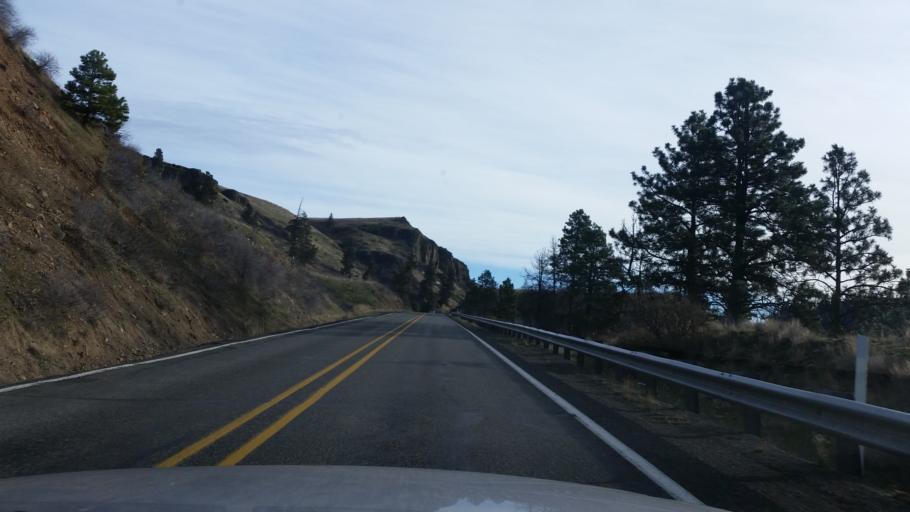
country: US
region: Washington
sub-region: Kittitas County
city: Cle Elum
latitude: 47.1303
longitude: -120.7712
